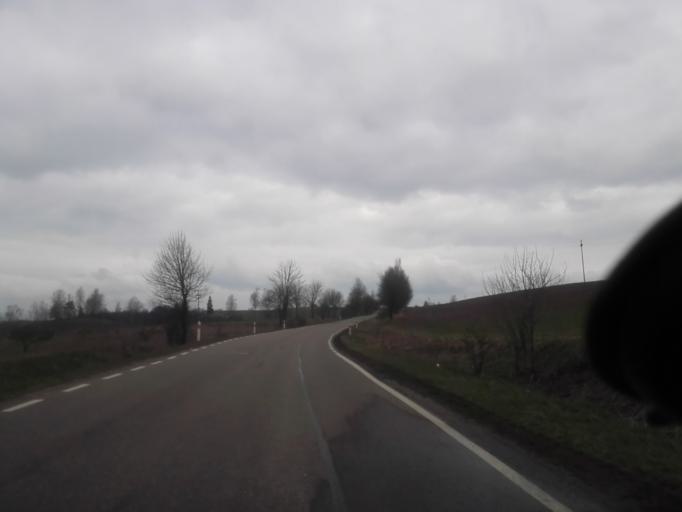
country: PL
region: Podlasie
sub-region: Suwalki
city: Suwalki
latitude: 54.2329
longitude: 22.9130
